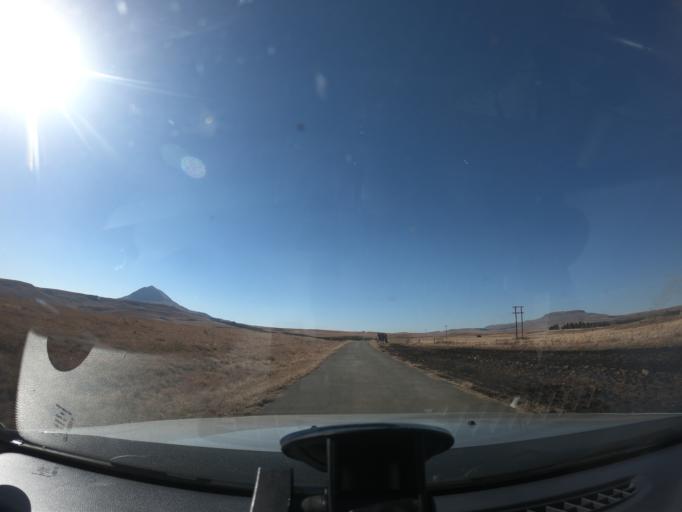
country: ZA
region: KwaZulu-Natal
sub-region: uMgungundlovu District Municipality
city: Impendle
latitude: -29.3885
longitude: 29.7326
